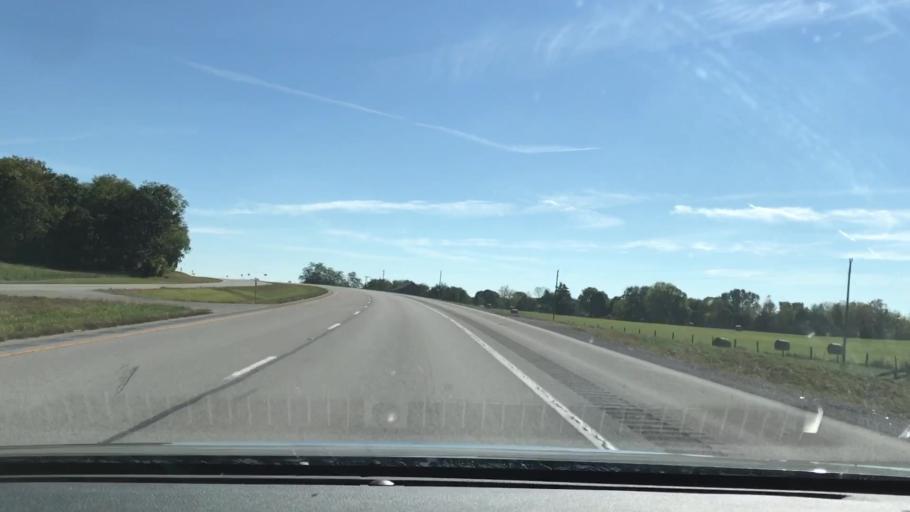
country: US
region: Kentucky
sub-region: Todd County
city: Elkton
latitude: 36.8098
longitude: -87.1344
